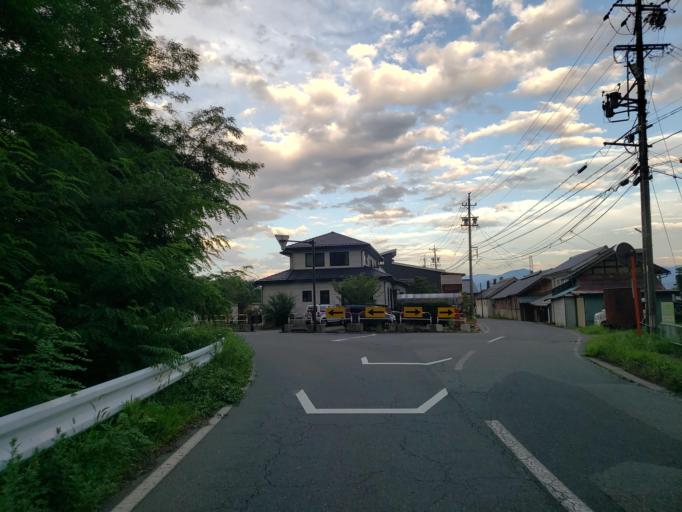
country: JP
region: Nagano
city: Nagano-shi
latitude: 36.6206
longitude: 138.1318
